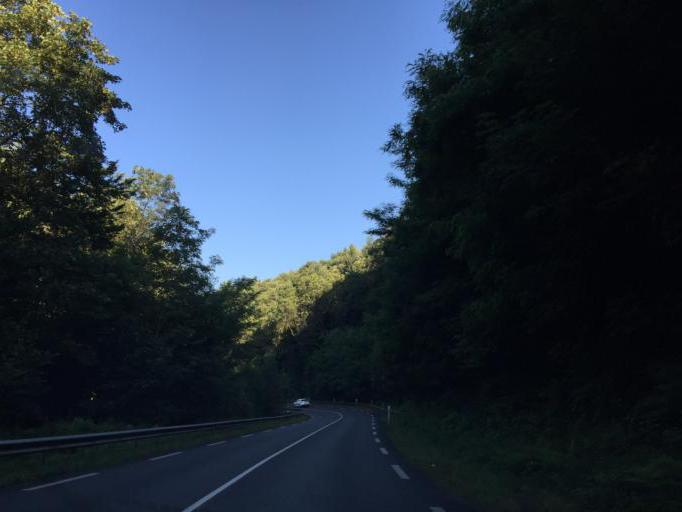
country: FR
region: Rhone-Alpes
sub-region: Departement de la Loire
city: Sorbiers
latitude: 45.4770
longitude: 4.4671
